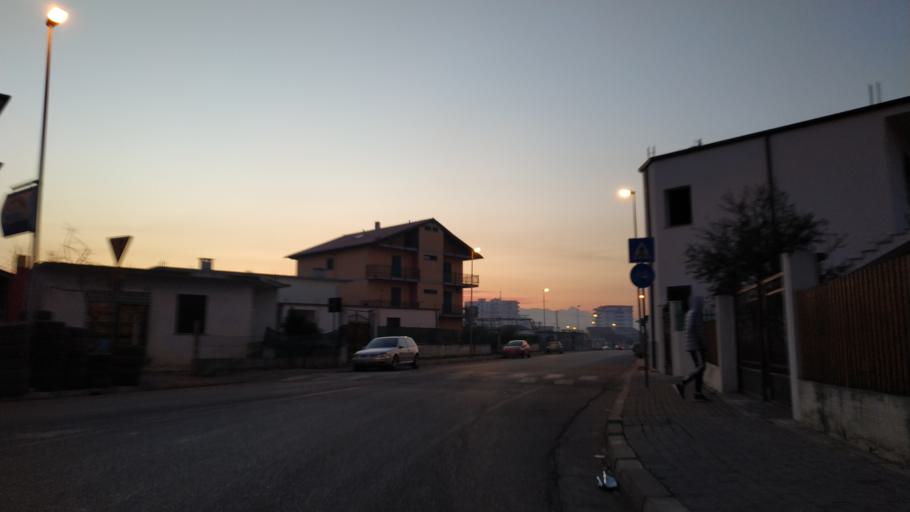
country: AL
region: Shkoder
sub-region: Rrethi i Shkodres
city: Shkoder
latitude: 42.0788
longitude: 19.5219
